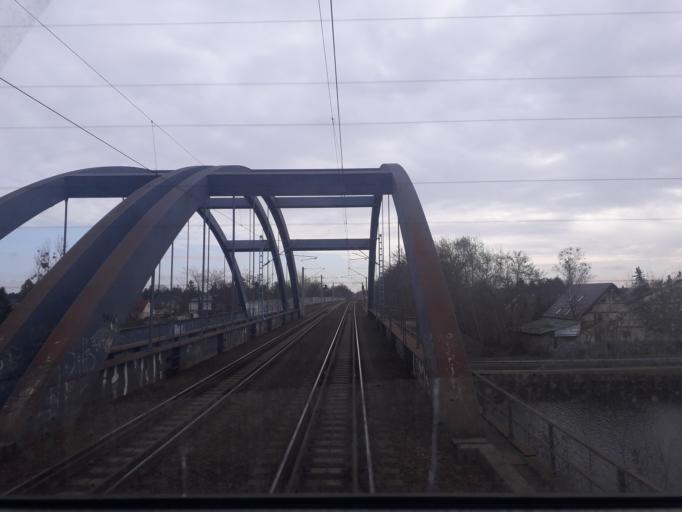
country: DE
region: Brandenburg
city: Brieselang
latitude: 52.5894
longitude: 12.9751
